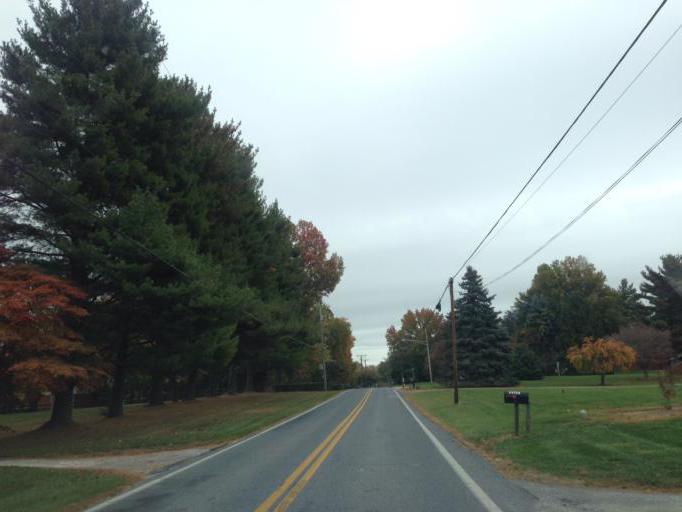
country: US
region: Maryland
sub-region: Howard County
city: Highland
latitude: 39.2740
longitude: -76.9587
